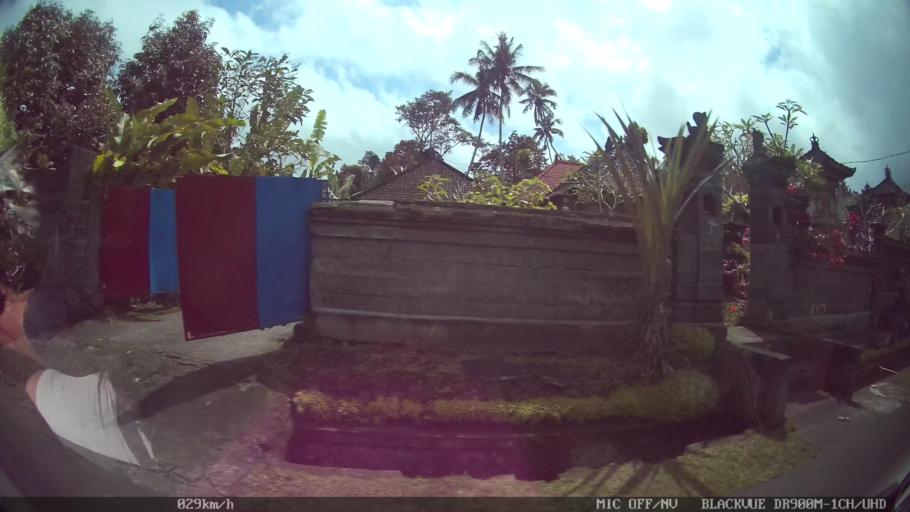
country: ID
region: Bali
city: Banjar Susut Kaja
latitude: -8.4434
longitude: 115.3297
